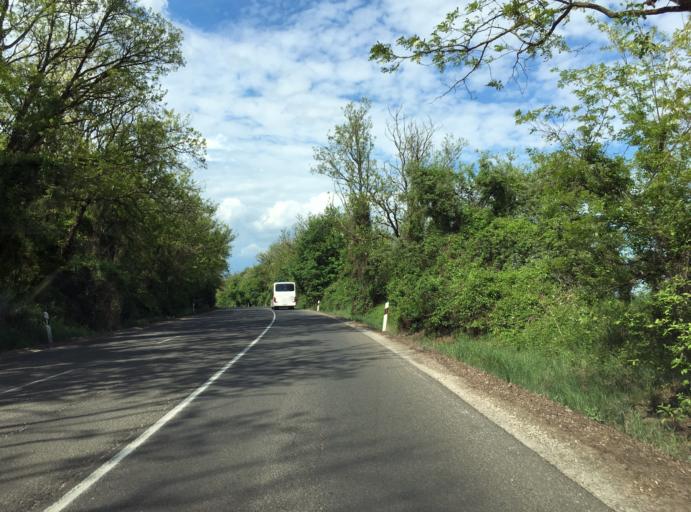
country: HU
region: Pest
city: Bag
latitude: 47.6360
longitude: 19.4610
